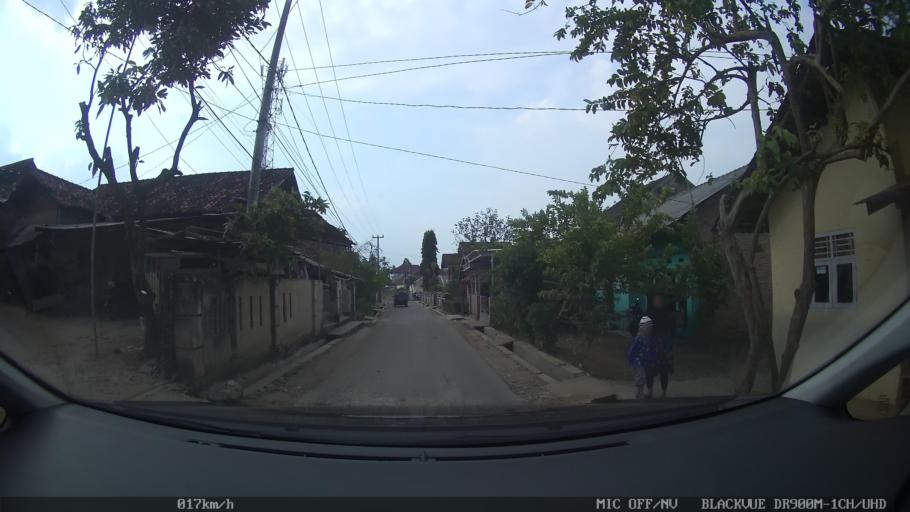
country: ID
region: Lampung
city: Kedaton
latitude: -5.3721
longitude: 105.2182
